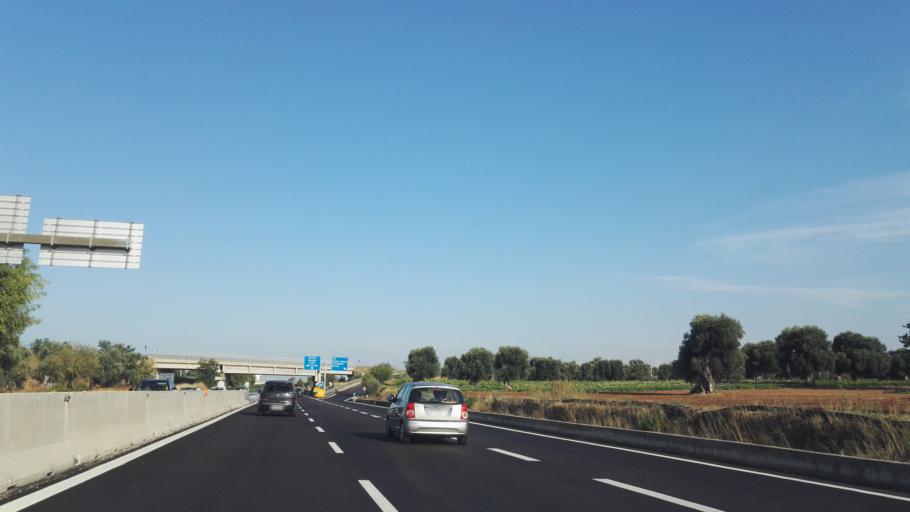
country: IT
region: Apulia
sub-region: Provincia di Brindisi
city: Fasano
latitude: 40.8368
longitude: 17.3844
